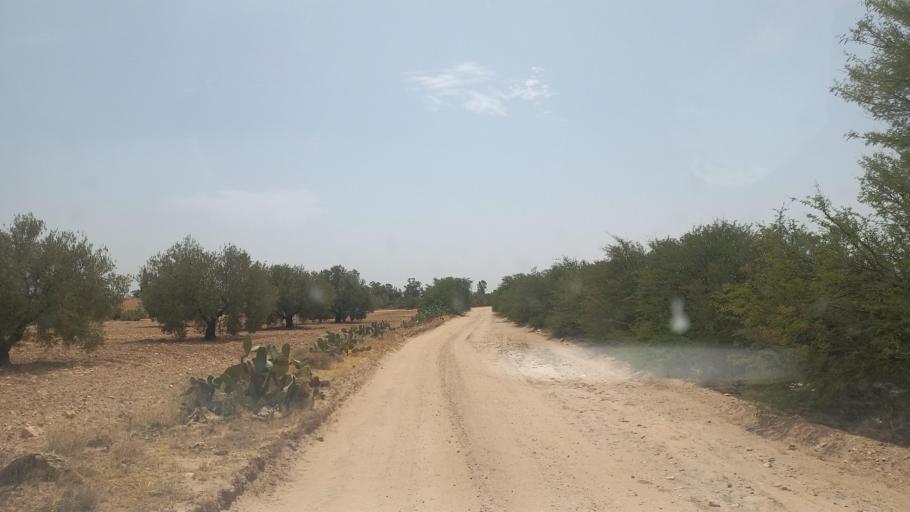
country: TN
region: Al Qasrayn
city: Kasserine
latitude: 35.2544
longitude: 9.0073
